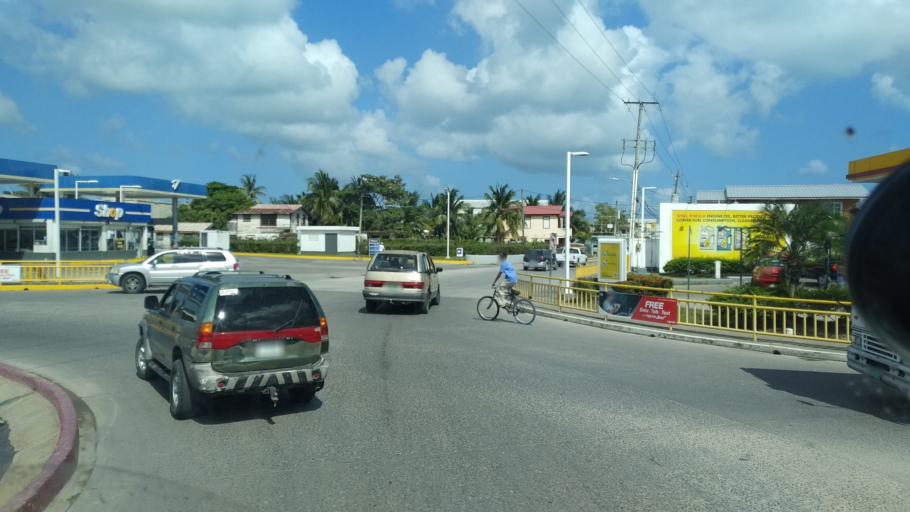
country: BZ
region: Belize
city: Belize City
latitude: 17.4956
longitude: -88.1990
